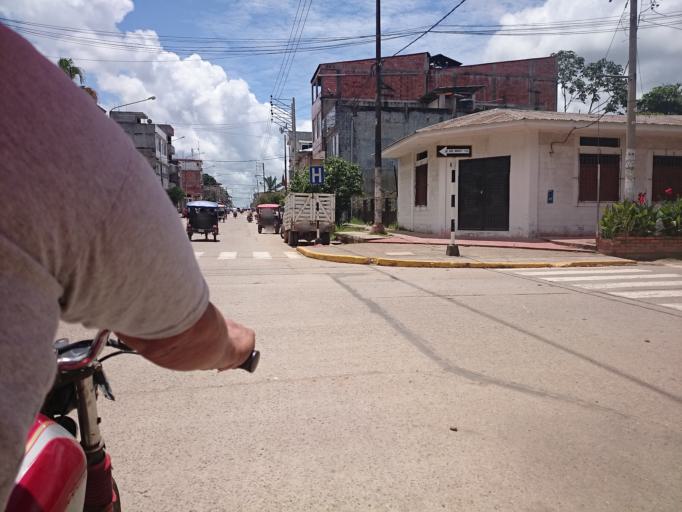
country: PE
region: Ucayali
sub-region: Provincia de Coronel Portillo
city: Pucallpa
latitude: -8.3798
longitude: -74.5306
